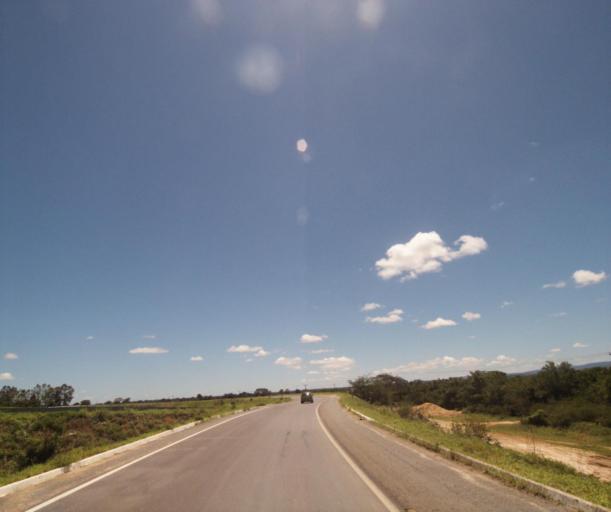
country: BR
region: Bahia
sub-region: Carinhanha
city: Carinhanha
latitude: -14.3291
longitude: -43.7656
